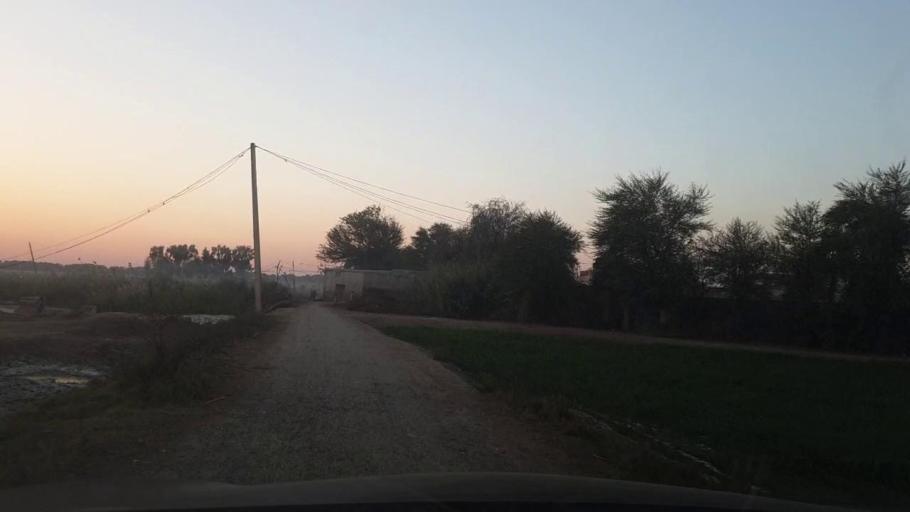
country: PK
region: Sindh
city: Ubauro
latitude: 28.1772
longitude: 69.6335
